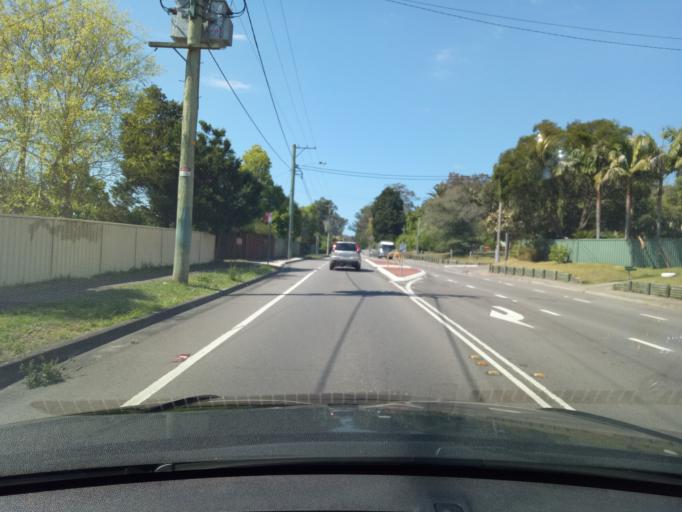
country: AU
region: New South Wales
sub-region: Gosford Shire
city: Narara
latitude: -33.4048
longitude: 151.3383
